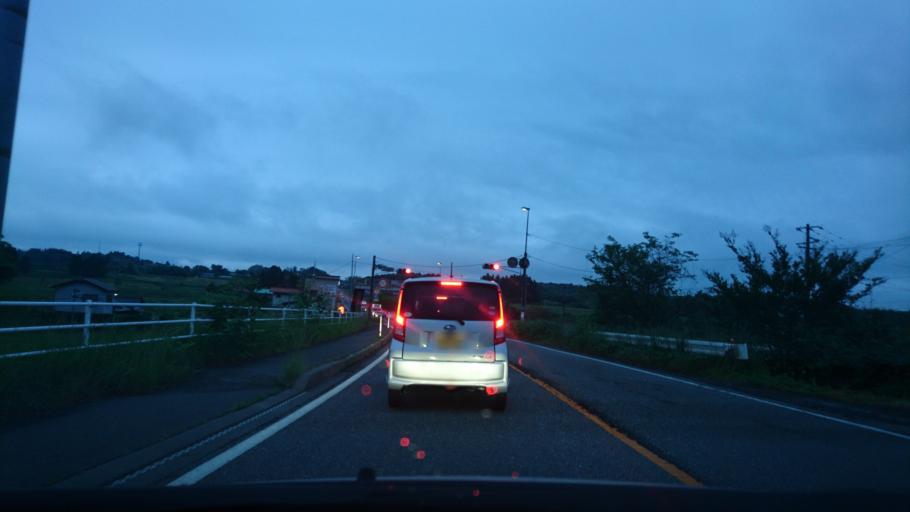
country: JP
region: Iwate
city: Ichinoseki
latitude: 38.8522
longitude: 141.0970
